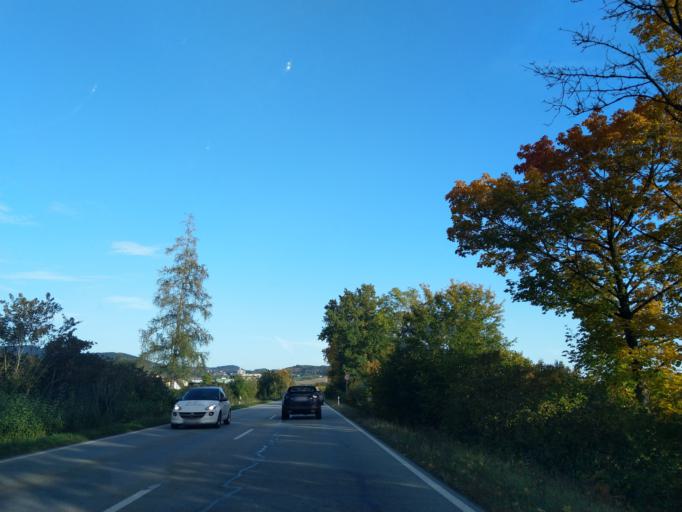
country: DE
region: Bavaria
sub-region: Lower Bavaria
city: Deggendorf
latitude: 48.8352
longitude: 12.9382
